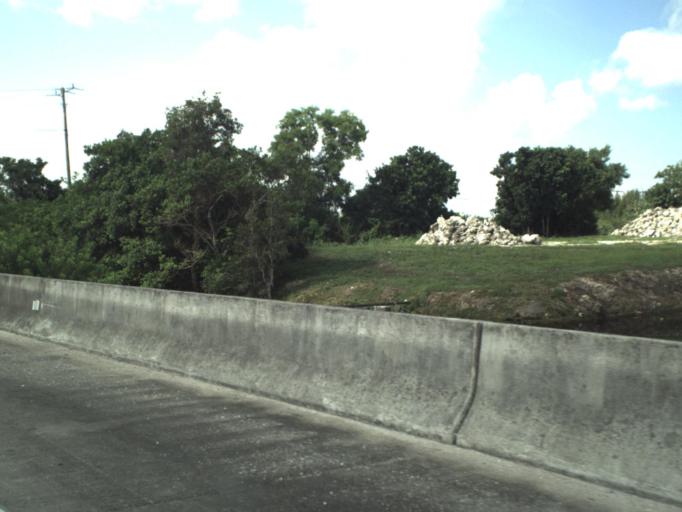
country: US
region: Florida
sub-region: Broward County
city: Weston
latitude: 26.0615
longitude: -80.4345
